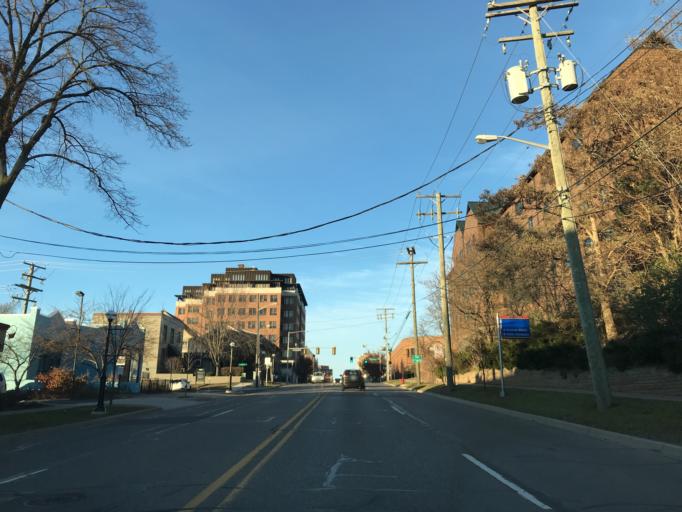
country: US
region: Michigan
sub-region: Washtenaw County
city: Ann Arbor
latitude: 42.2756
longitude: -83.7488
